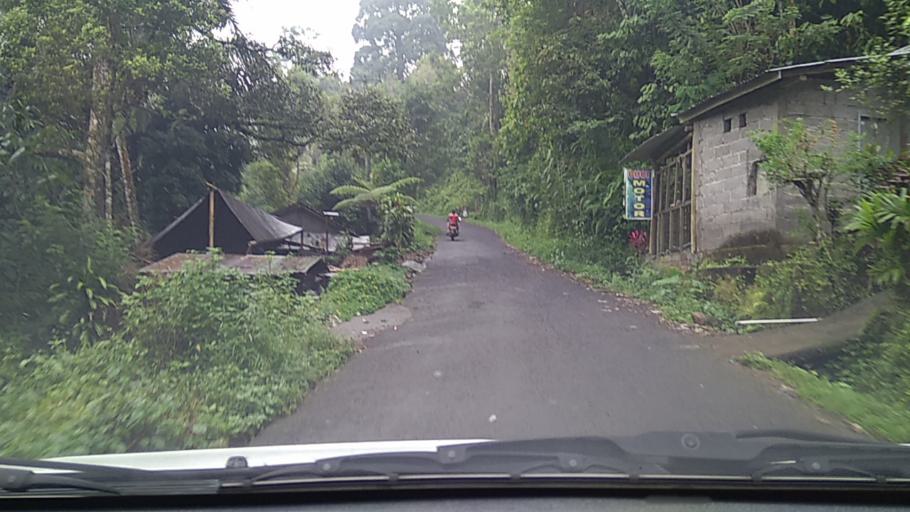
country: ID
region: Bali
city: Banjar Padangbulia
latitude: -8.1934
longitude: 115.1873
